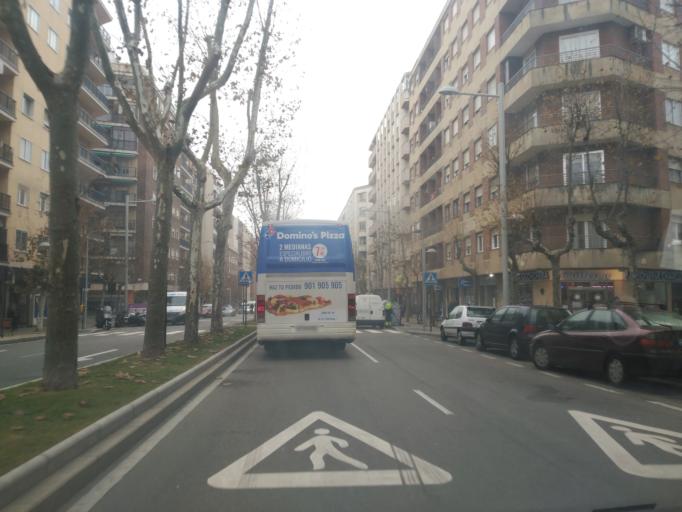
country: ES
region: Castille and Leon
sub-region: Provincia de Salamanca
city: Salamanca
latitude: 40.9709
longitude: -5.6563
